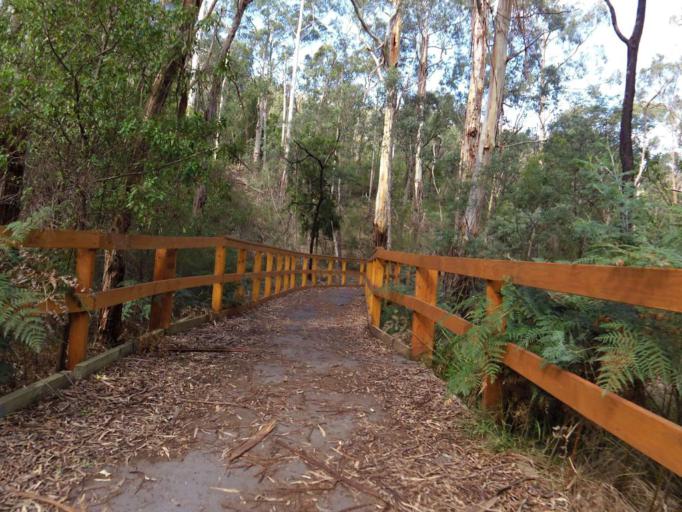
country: AU
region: Victoria
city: Mitcham
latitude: -37.7961
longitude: 145.2038
